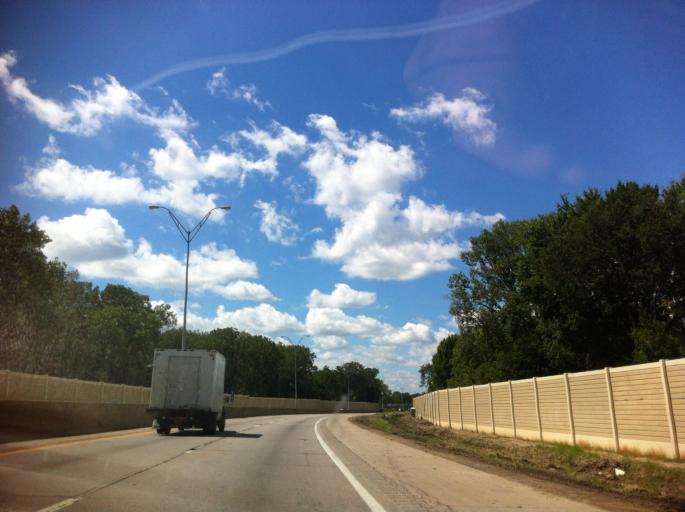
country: US
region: Ohio
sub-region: Lucas County
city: Ottawa Hills
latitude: 41.6880
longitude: -83.6538
